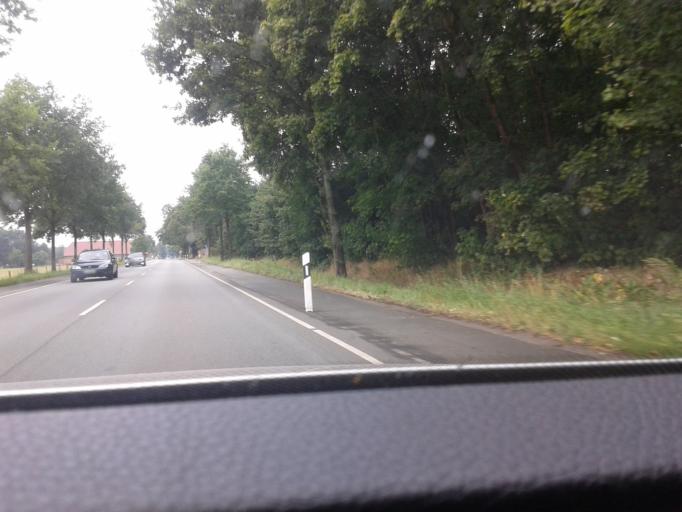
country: DE
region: Lower Saxony
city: Osloss
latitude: 52.4680
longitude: 10.6916
